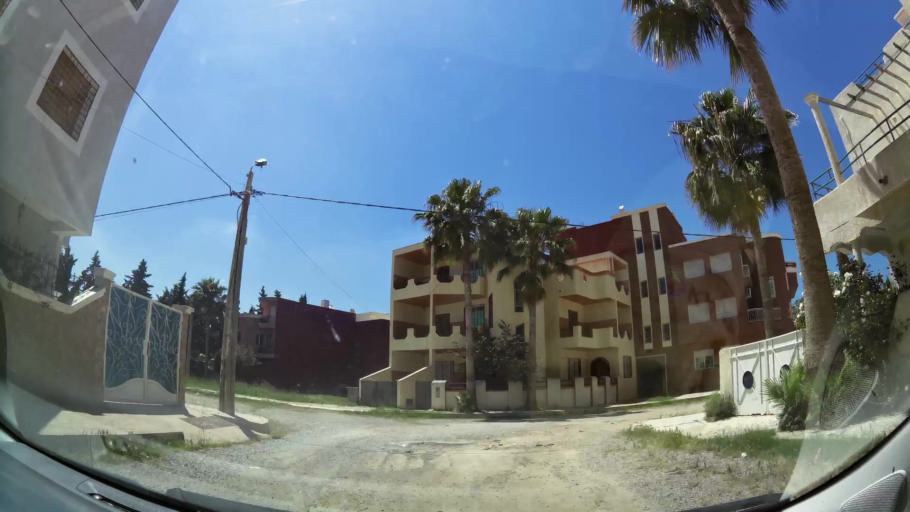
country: MA
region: Oriental
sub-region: Berkane-Taourirt
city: Madagh
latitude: 35.0769
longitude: -2.2152
